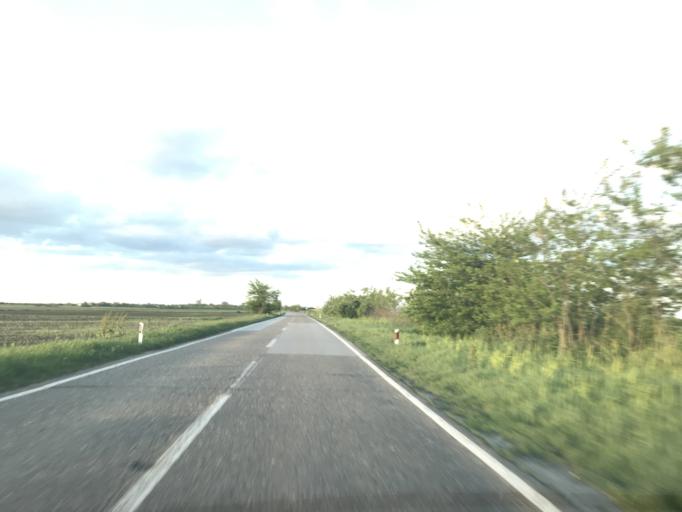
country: RS
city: Cestereg
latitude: 45.5476
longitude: 20.5118
